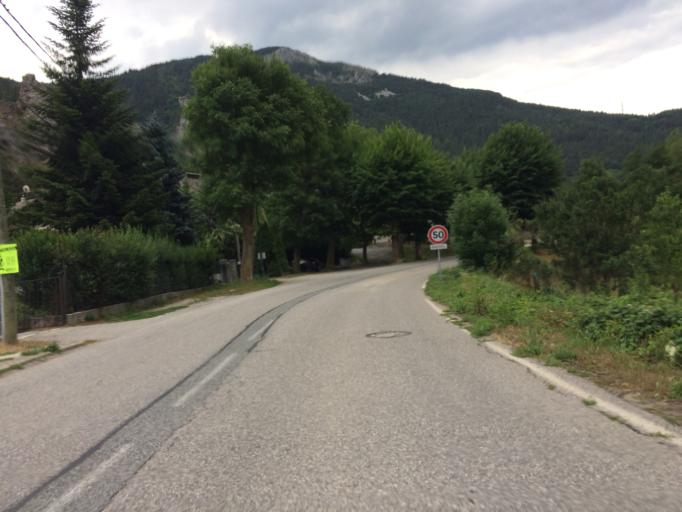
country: FR
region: Provence-Alpes-Cote d'Azur
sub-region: Departement des Alpes-Maritimes
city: Tende
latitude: 44.0794
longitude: 7.5986
